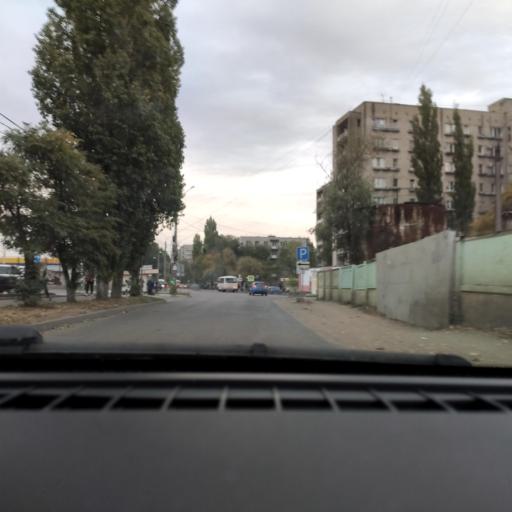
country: RU
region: Voronezj
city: Maslovka
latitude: 51.6352
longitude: 39.2729
